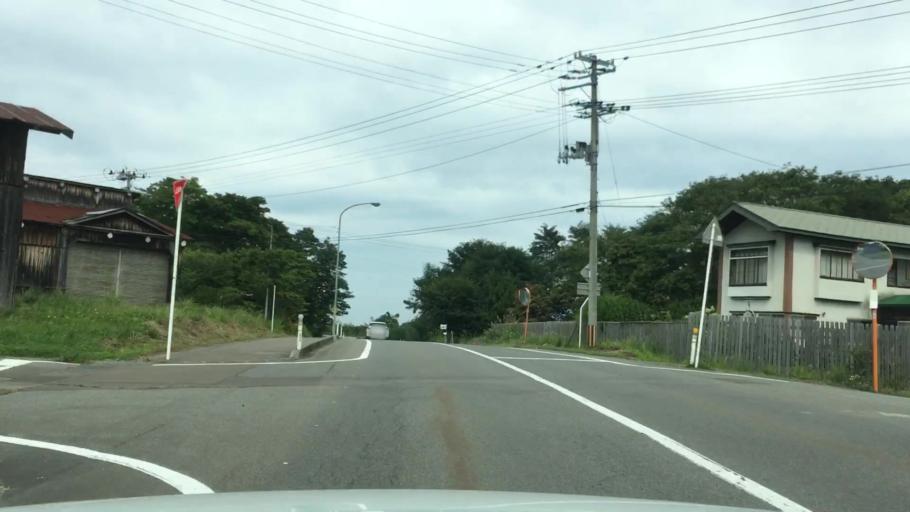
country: JP
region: Aomori
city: Shimokizukuri
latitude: 40.7579
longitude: 140.2305
